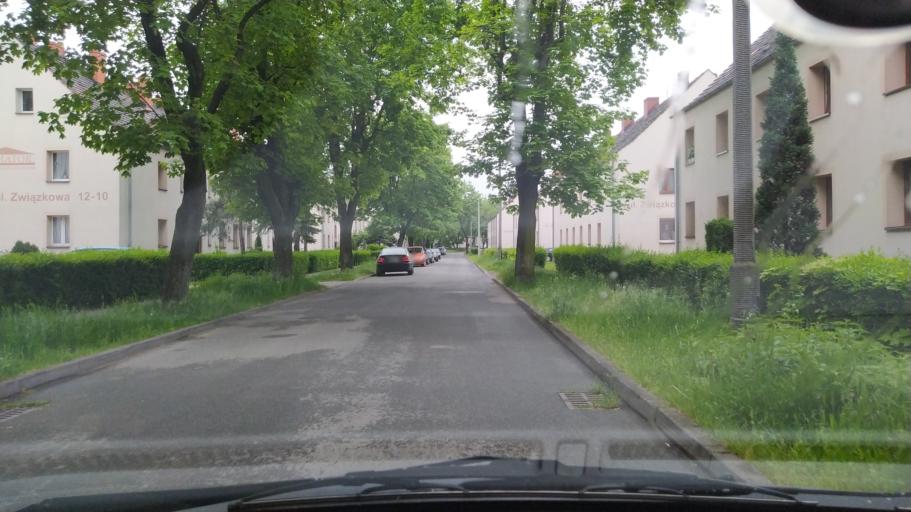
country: PL
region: Silesian Voivodeship
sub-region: Gliwice
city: Gliwice
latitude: 50.2946
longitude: 18.7237
